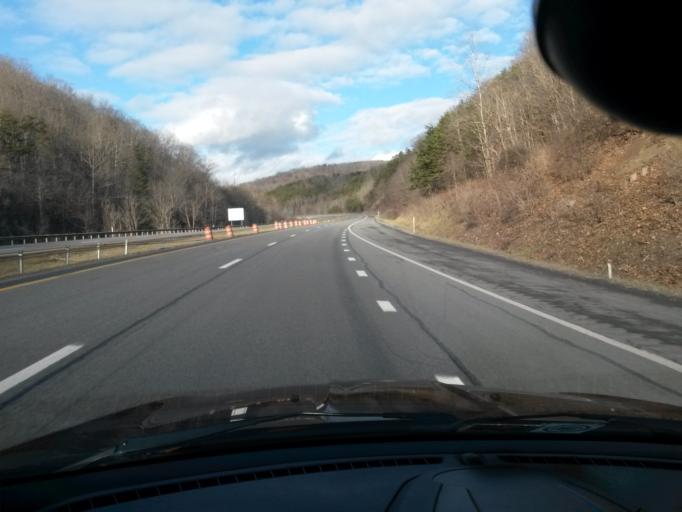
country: US
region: West Virginia
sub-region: Mercer County
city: Princeton
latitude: 37.3185
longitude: -81.0591
